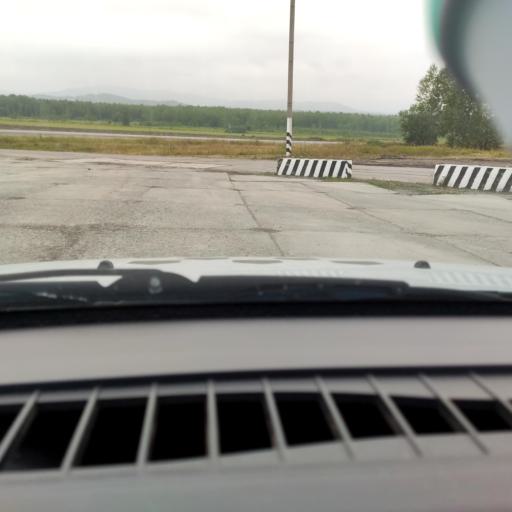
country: RU
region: Chelyabinsk
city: Miass
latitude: 54.9407
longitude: 60.0507
